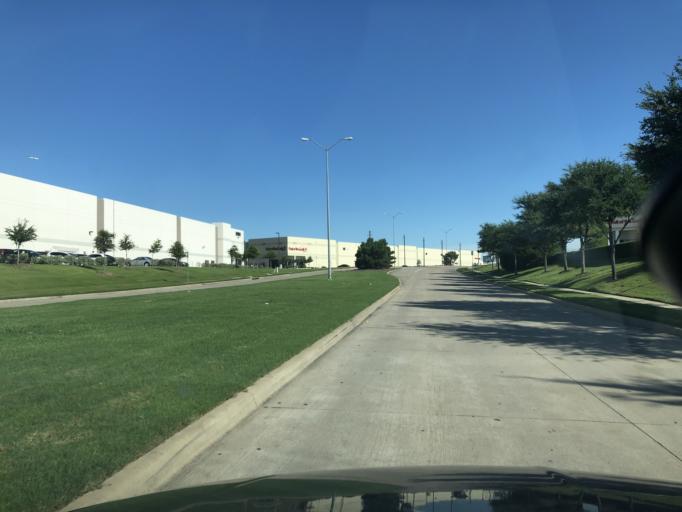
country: US
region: Texas
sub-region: Tarrant County
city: Euless
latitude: 32.8039
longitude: -97.0331
